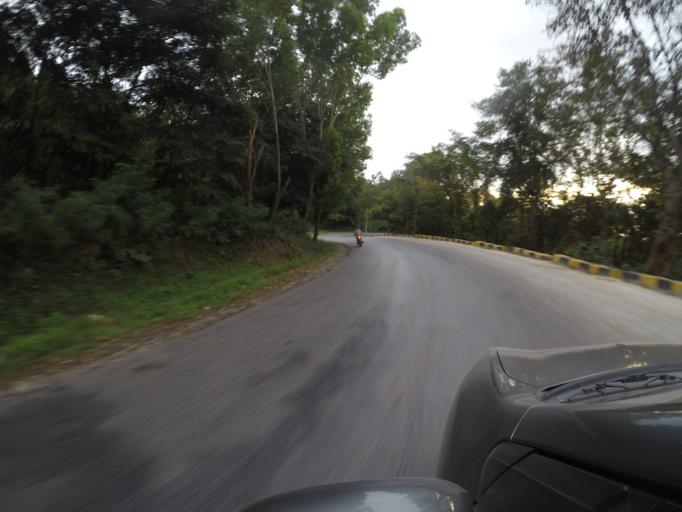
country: MM
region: Shan
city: Taunggyi
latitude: 20.8110
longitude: 97.0258
